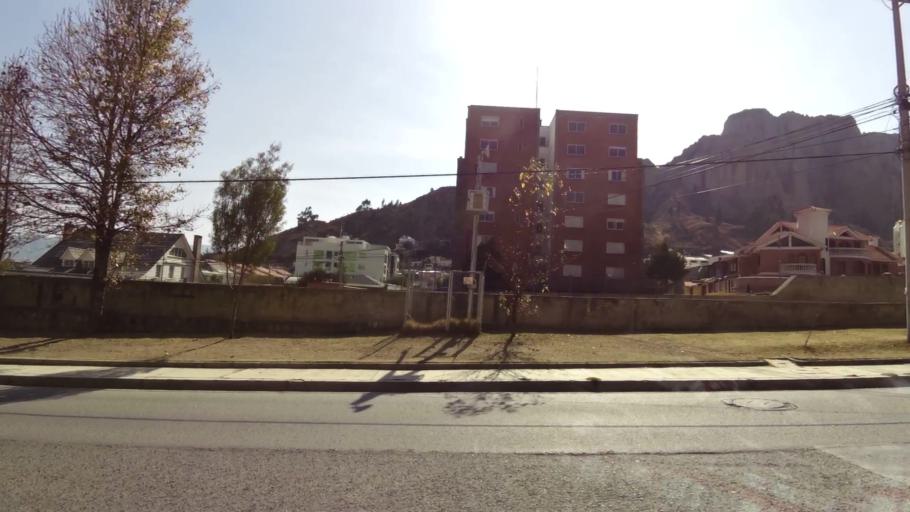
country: BO
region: La Paz
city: La Paz
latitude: -16.5238
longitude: -68.0670
